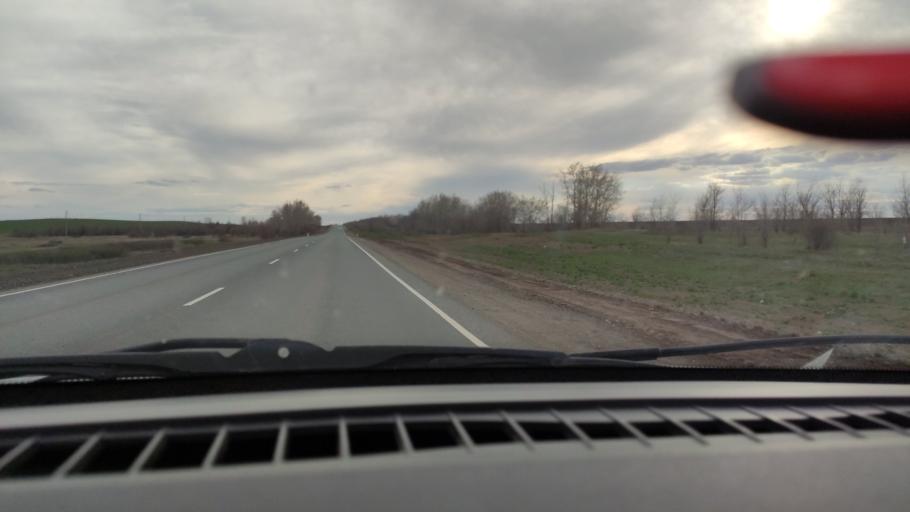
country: RU
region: Orenburg
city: Sakmara
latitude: 52.3079
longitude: 55.4492
